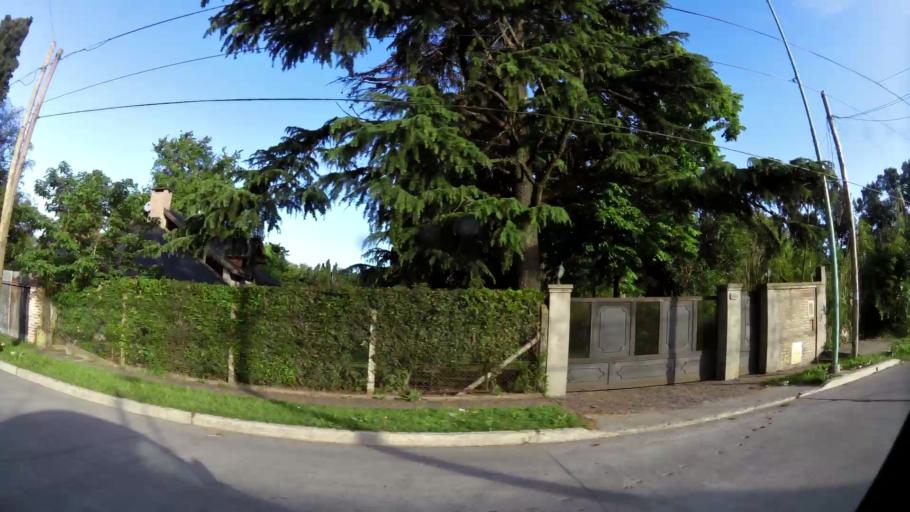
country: AR
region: Buenos Aires
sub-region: Partido de Quilmes
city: Quilmes
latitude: -34.8080
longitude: -58.2085
